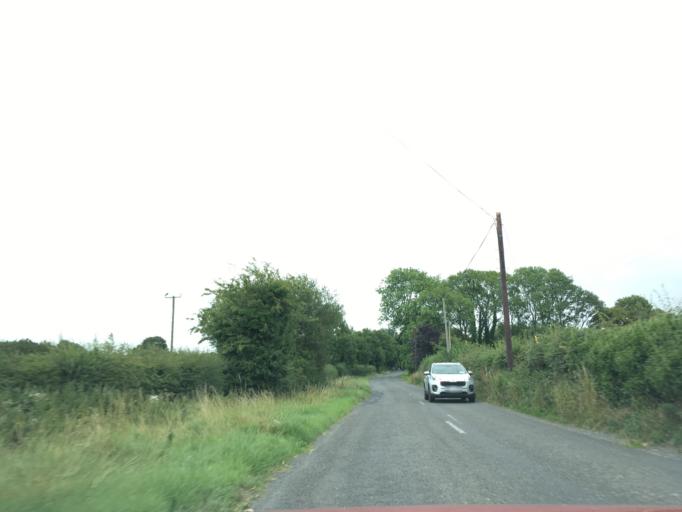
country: IE
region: Munster
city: Cashel
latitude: 52.4758
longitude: -7.8827
